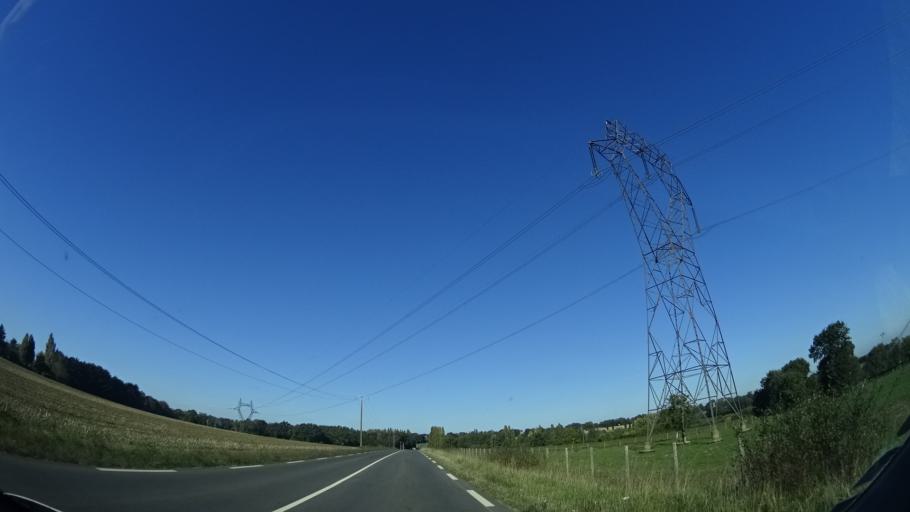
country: FR
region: Brittany
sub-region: Departement d'Ille-et-Vilaine
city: Saint-Gregoire
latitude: 48.1810
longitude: -1.6942
